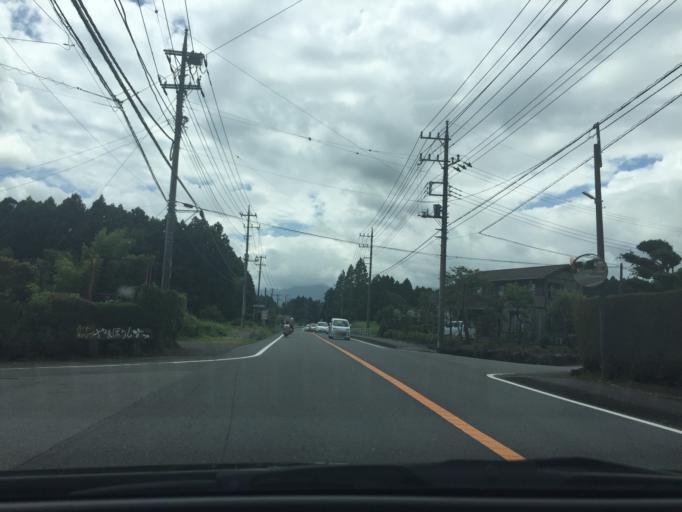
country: JP
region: Shizuoka
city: Gotemba
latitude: 35.2881
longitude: 138.8887
